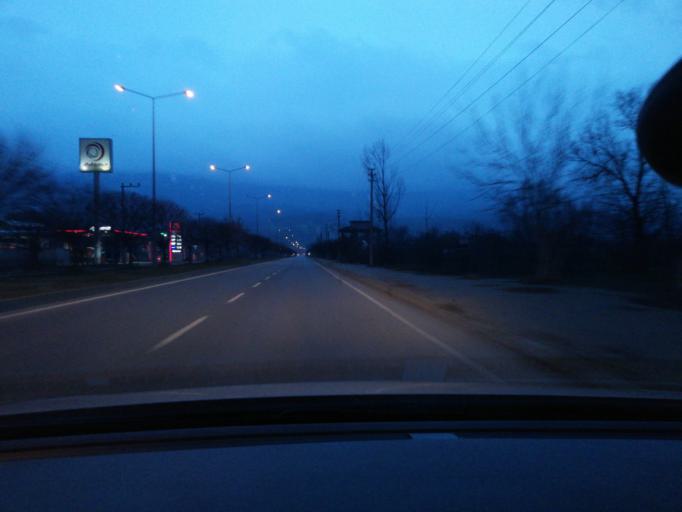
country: TR
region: Bolu
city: Bolu
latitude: 40.7039
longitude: 31.6177
